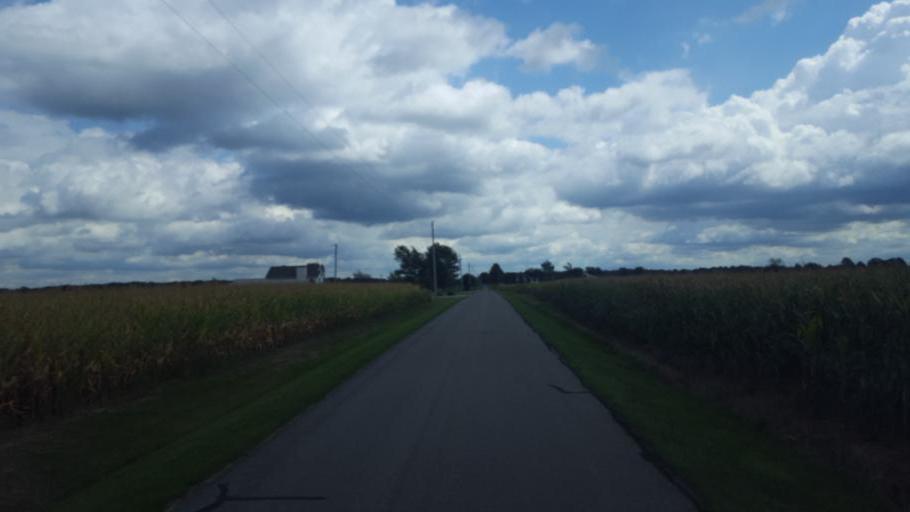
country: US
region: Ohio
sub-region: Huron County
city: Willard
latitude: 41.1152
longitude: -82.7660
